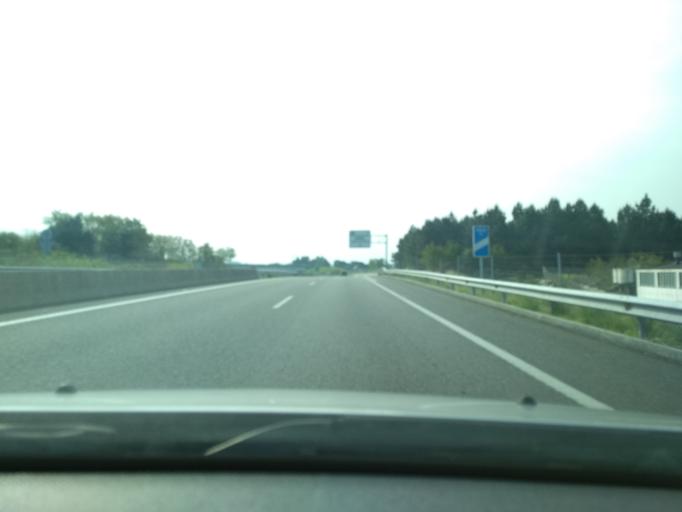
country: ES
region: Galicia
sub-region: Provincia da Coruna
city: Rianxo
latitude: 42.6722
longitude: -8.8297
